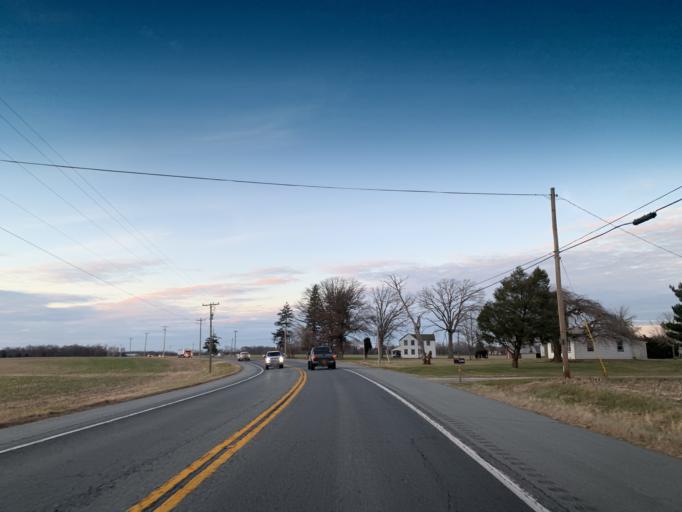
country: US
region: Delaware
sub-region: New Castle County
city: Middletown
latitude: 39.4380
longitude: -75.8619
